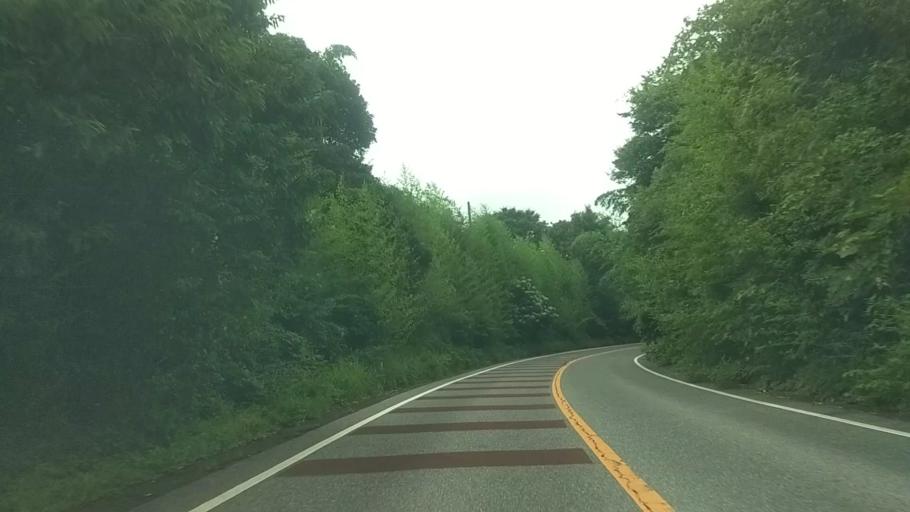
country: JP
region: Chiba
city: Kimitsu
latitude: 35.2362
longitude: 140.0066
